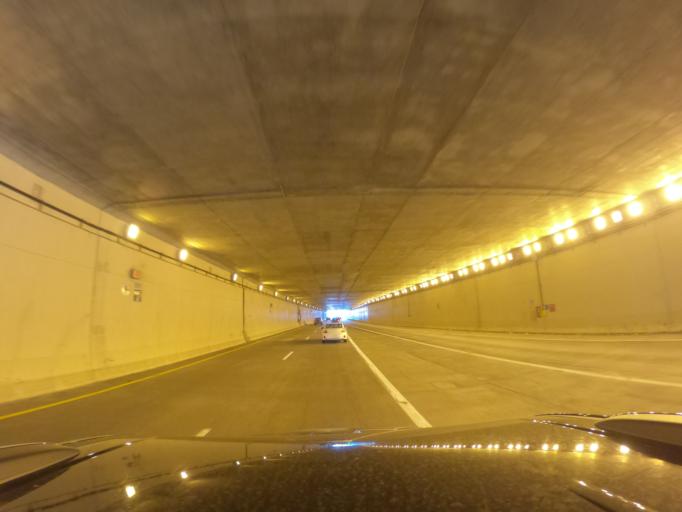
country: US
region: New Jersey
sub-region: Mercer County
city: Trenton
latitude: 40.1962
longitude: -74.7593
